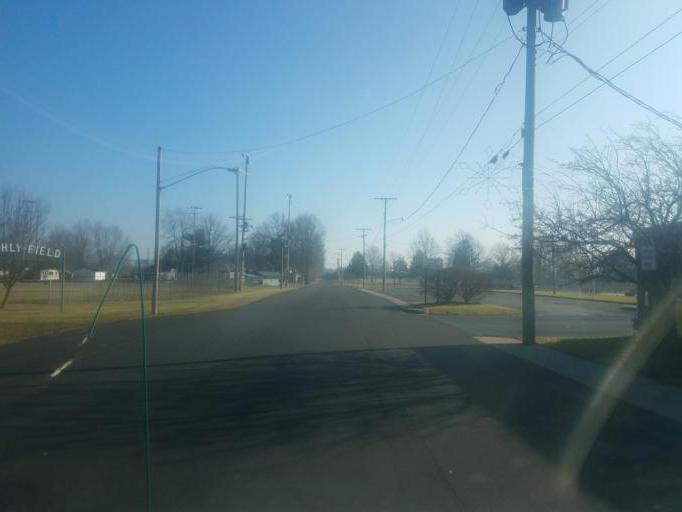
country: US
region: Ohio
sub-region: Seneca County
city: Tiffin
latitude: 41.0476
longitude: -83.0145
